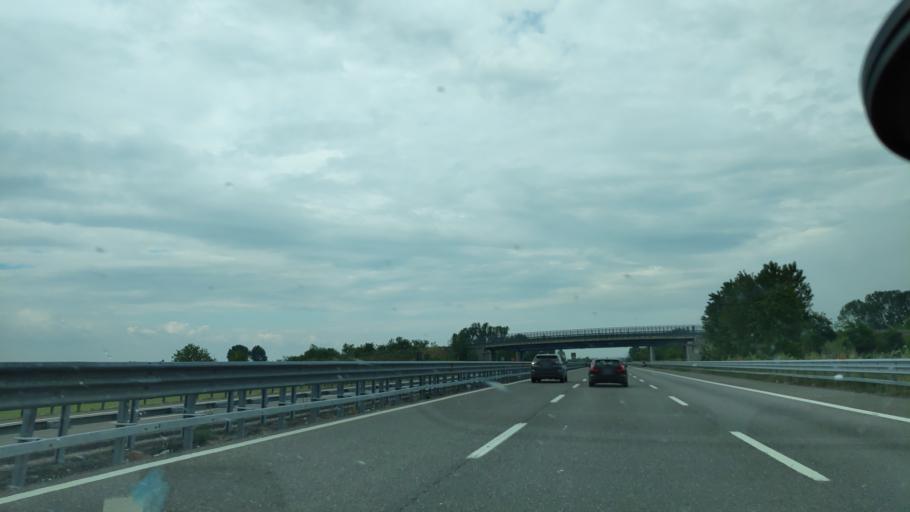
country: IT
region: Piedmont
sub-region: Provincia di Alessandria
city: Castelnuovo Scrivia
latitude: 44.9606
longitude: 8.8801
